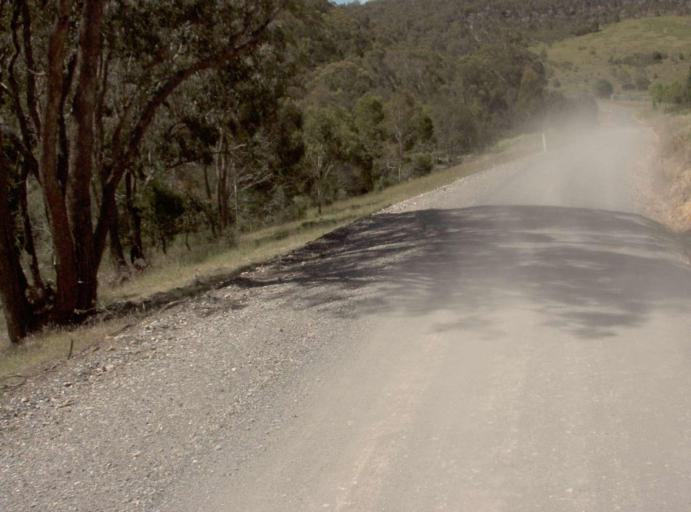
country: AU
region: New South Wales
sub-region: Bombala
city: Bombala
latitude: -37.1349
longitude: 148.6619
